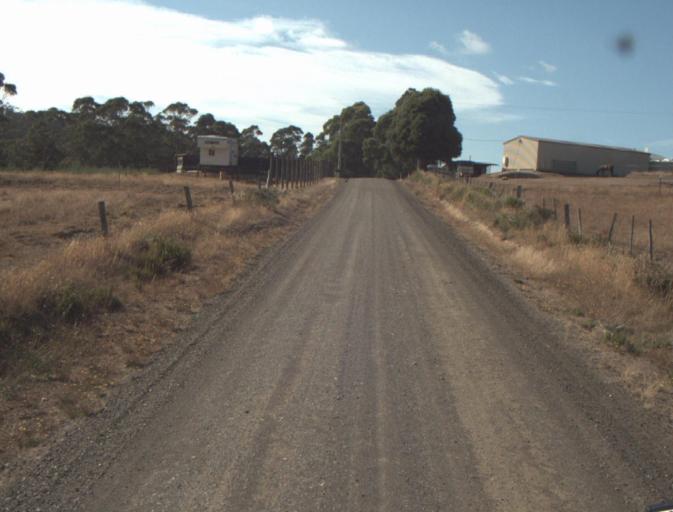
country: AU
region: Tasmania
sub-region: Dorset
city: Bridport
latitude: -41.1529
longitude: 147.2308
